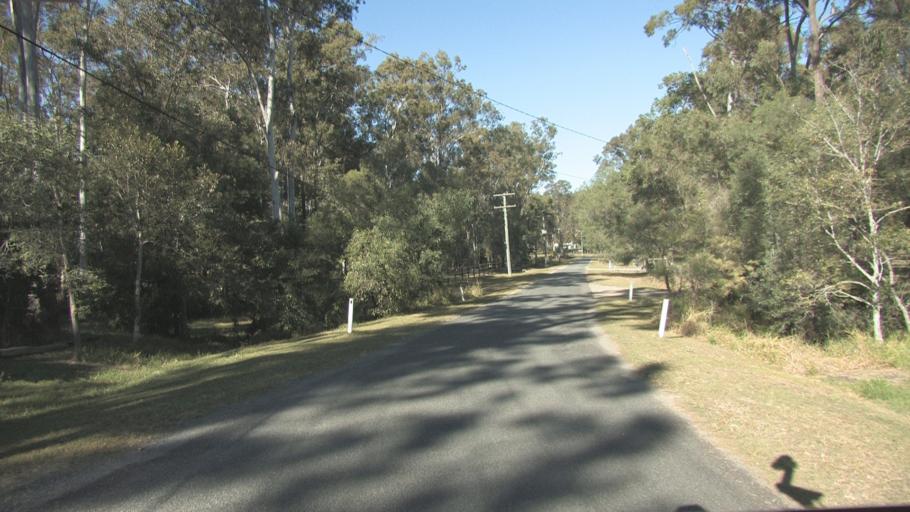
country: AU
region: Queensland
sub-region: Logan
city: Windaroo
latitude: -27.7912
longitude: 153.1470
